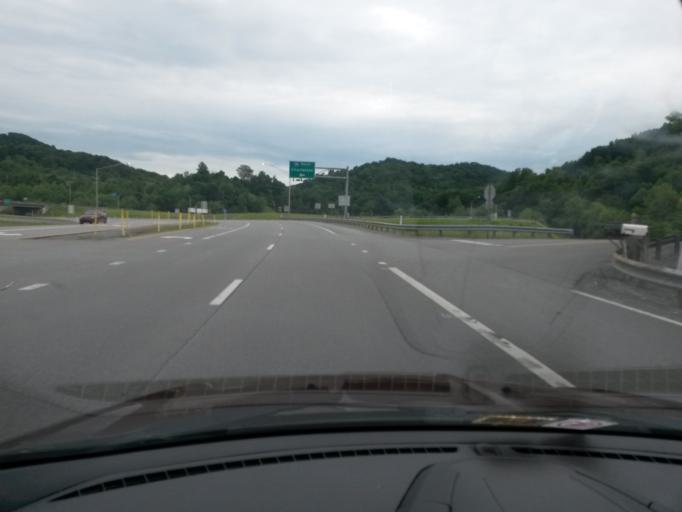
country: US
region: West Virginia
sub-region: Lewis County
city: Weston
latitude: 39.0241
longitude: -80.4296
